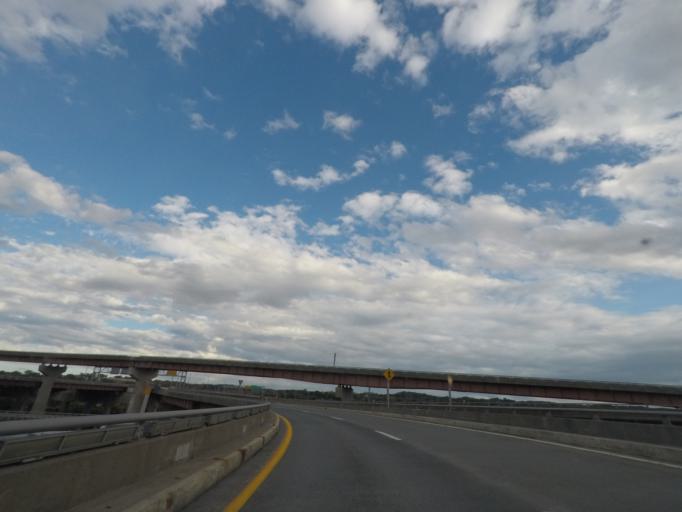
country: US
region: New York
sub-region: Rensselaer County
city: Rensselaer
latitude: 42.6432
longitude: -73.7514
